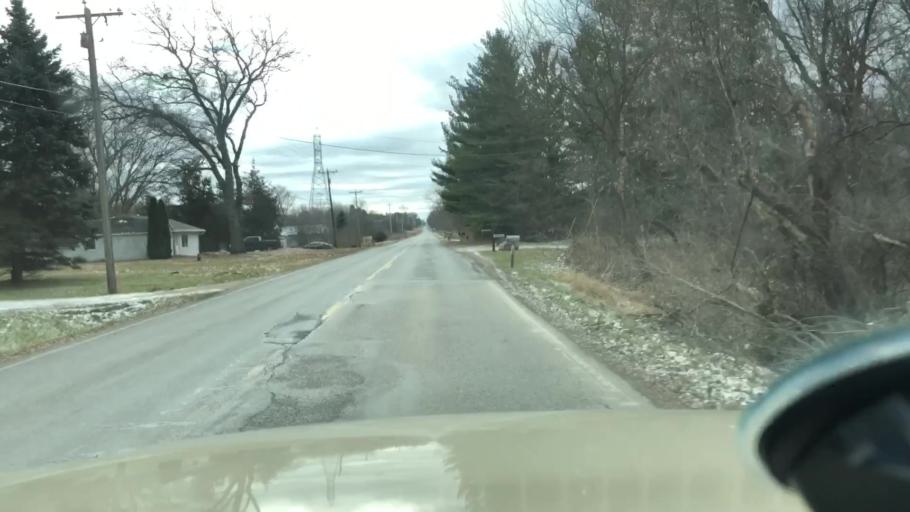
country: US
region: Michigan
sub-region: Jackson County
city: Jackson
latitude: 42.2709
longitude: -84.3650
